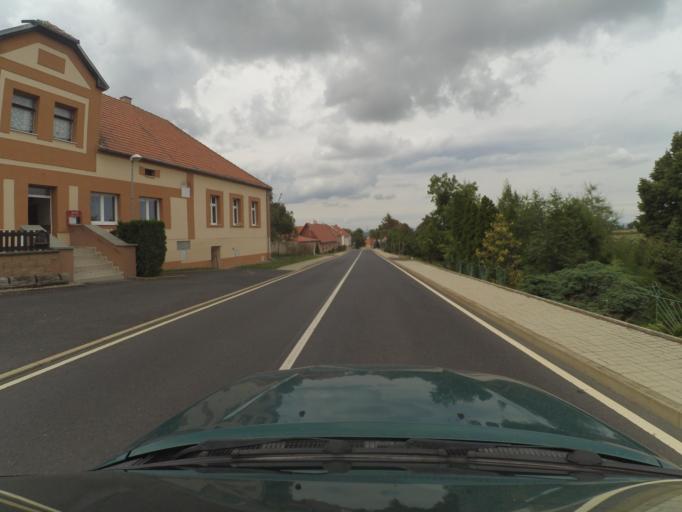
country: CZ
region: Ustecky
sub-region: Okres Louny
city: Louny
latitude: 50.2914
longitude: 13.7828
